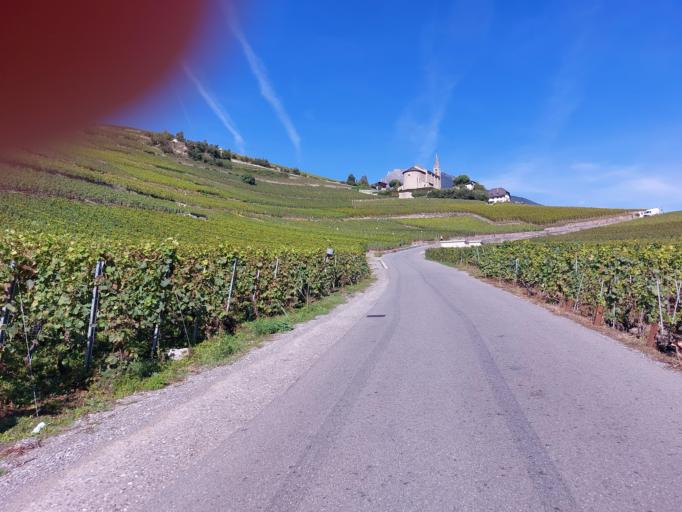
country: CH
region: Valais
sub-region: Conthey District
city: Conthey
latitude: 46.2314
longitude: 7.2980
